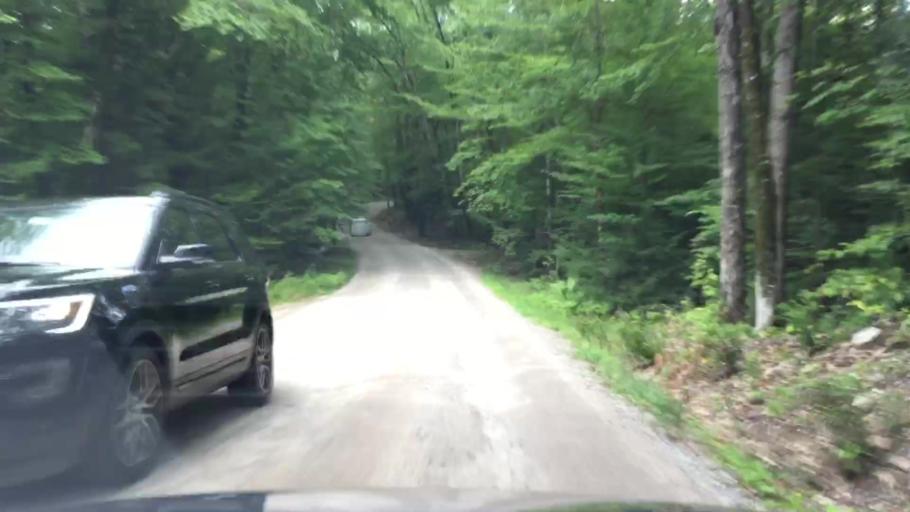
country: US
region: New Hampshire
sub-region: Carroll County
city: Sandwich
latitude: 43.7868
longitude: -71.4715
